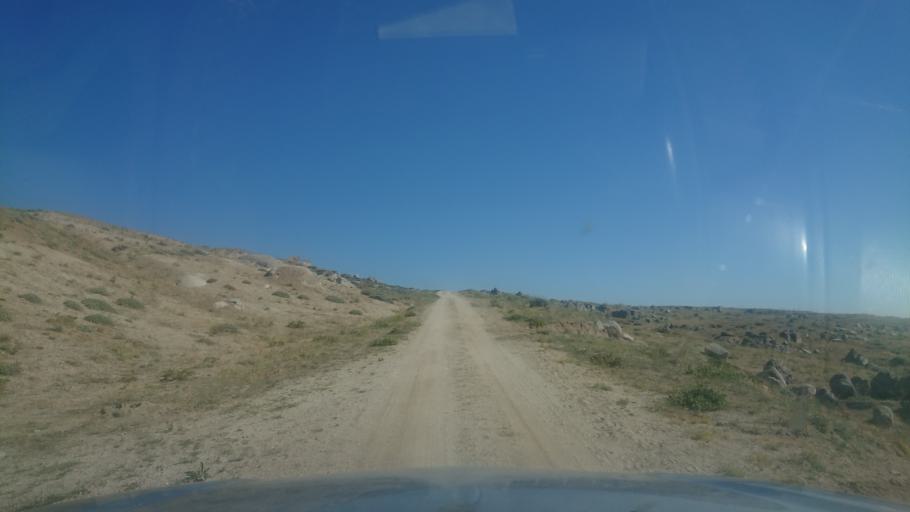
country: TR
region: Aksaray
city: Sariyahsi
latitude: 38.9214
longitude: 33.8524
